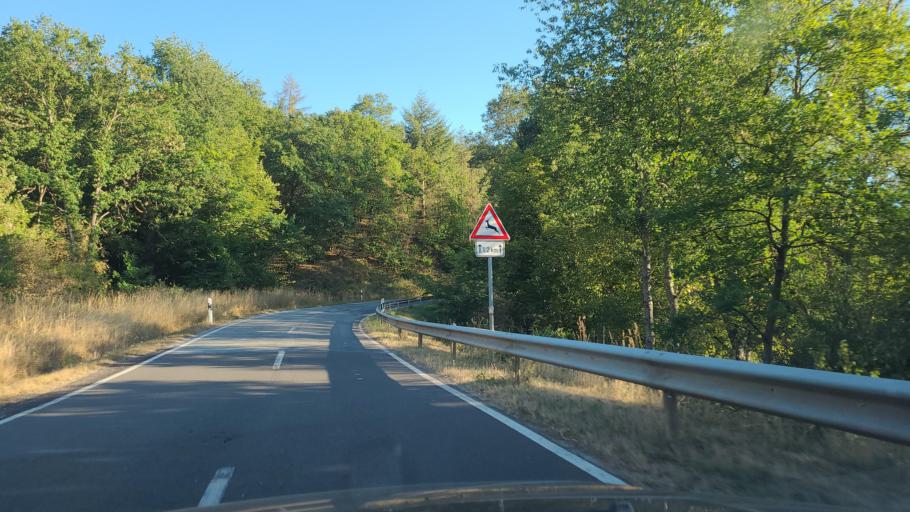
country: DE
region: Rheinland-Pfalz
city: Rivenich
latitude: 49.8642
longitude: 6.8500
